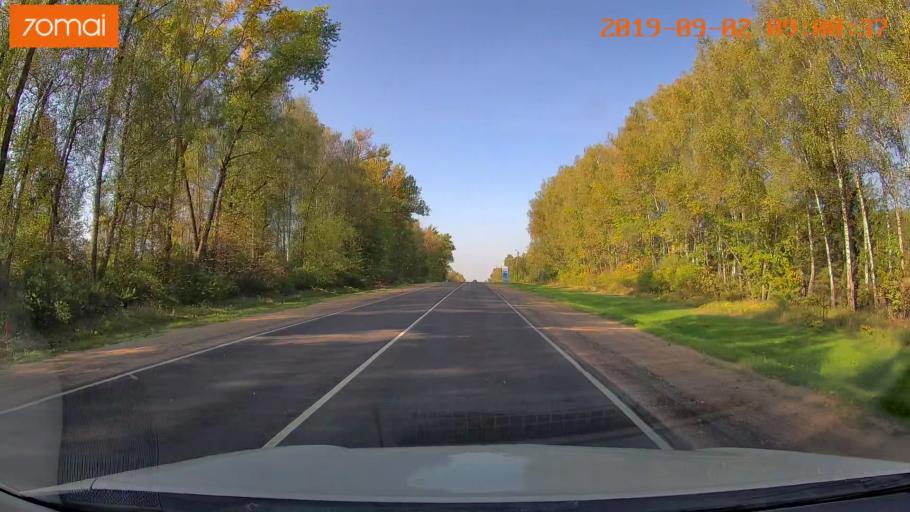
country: RU
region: Kaluga
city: Myatlevo
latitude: 54.9112
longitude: 35.7024
